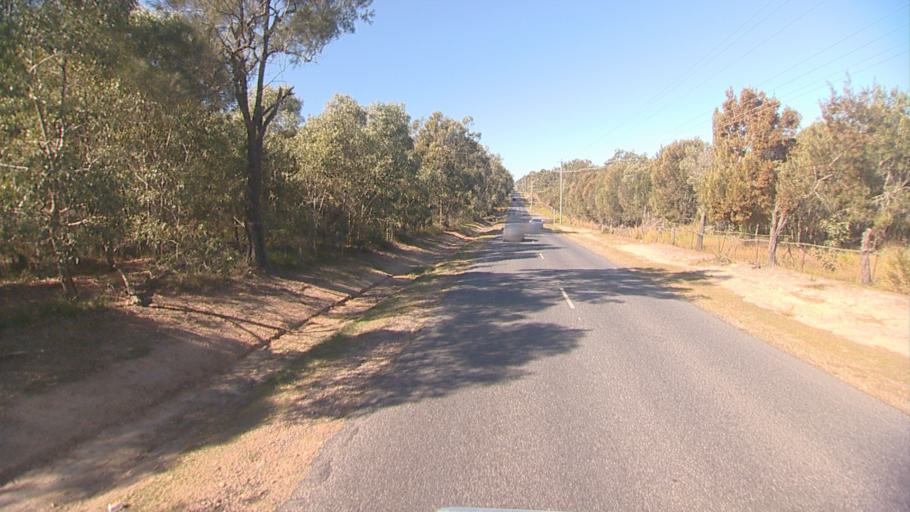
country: AU
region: Queensland
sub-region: Logan
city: Logan Reserve
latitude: -27.7110
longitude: 153.0946
